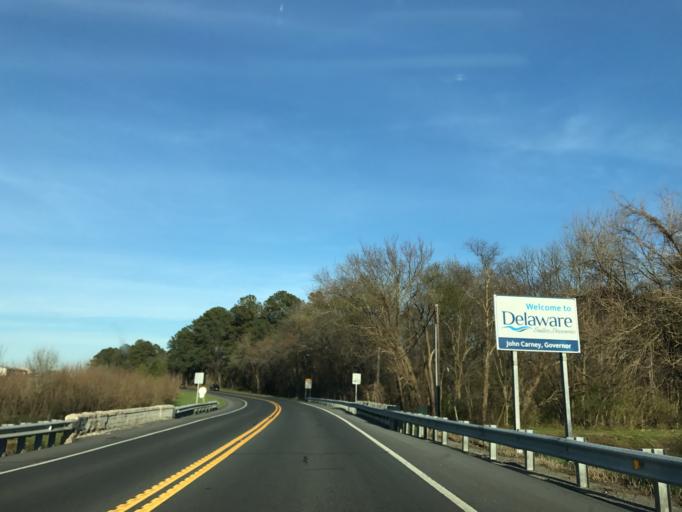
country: US
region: Maryland
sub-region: Caroline County
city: Greensboro
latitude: 39.1107
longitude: -75.7403
